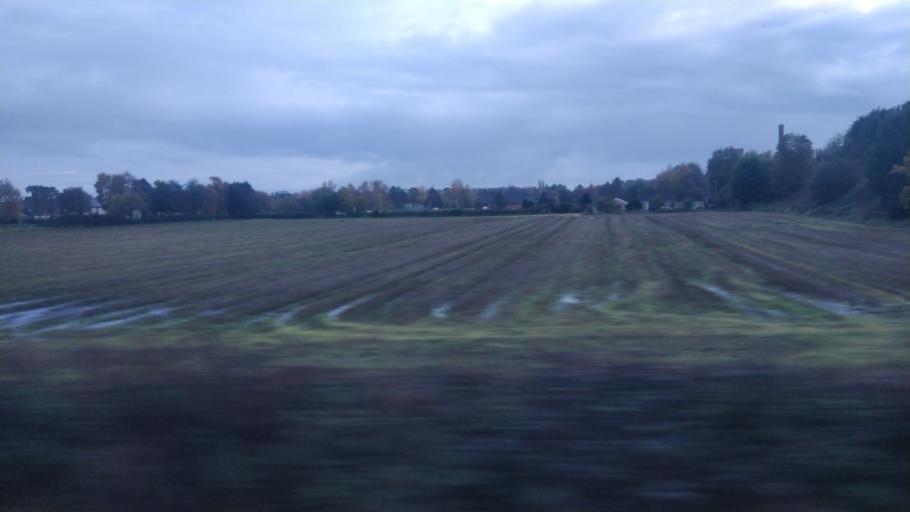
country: GB
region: England
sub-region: Lancashire
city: Ormskirk
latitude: 53.6038
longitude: -2.8330
